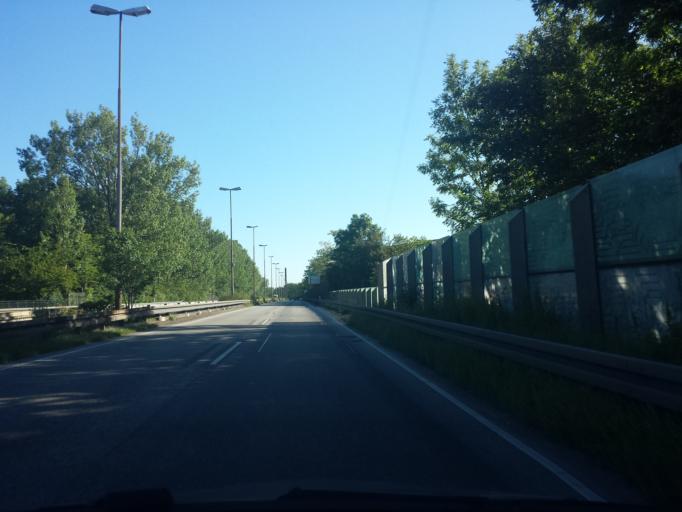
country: DK
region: Capital Region
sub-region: Ballerup Kommune
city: Ballerup
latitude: 55.7266
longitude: 12.3701
